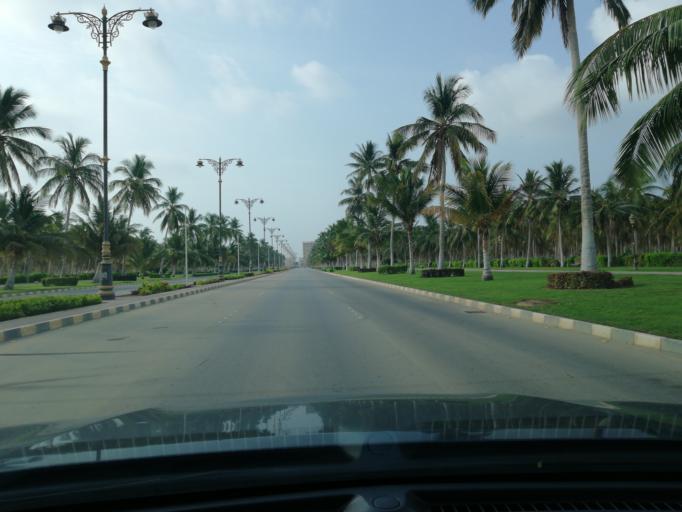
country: OM
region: Zufar
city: Salalah
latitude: 17.0313
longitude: 54.1094
